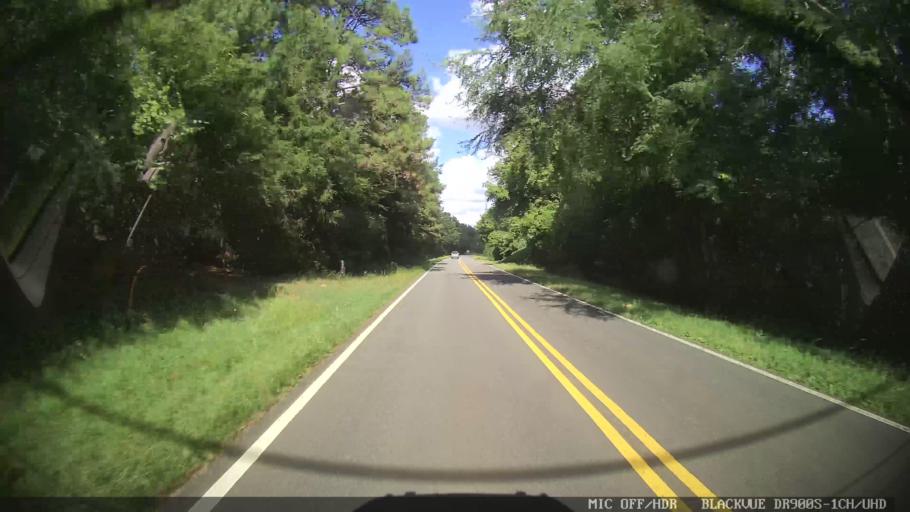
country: US
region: Georgia
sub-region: Bartow County
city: Euharlee
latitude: 34.1790
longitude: -85.0155
